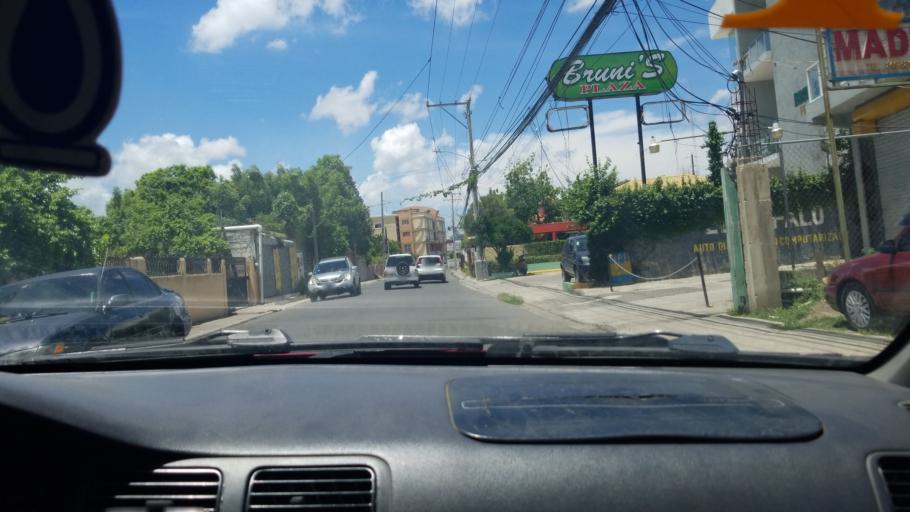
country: DO
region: Santiago
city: Santiago de los Caballeros
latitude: 19.4776
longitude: -70.6892
